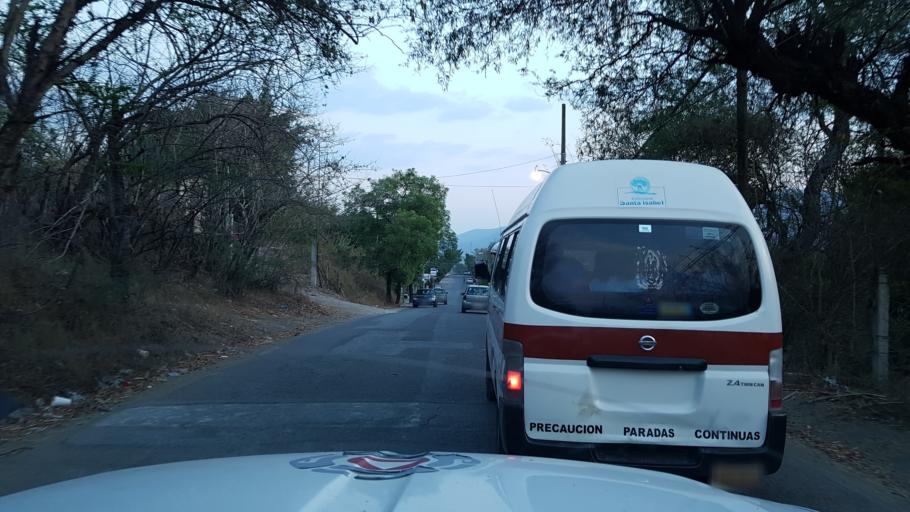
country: MX
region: Morelos
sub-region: Tlaltizapan de Zapata
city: Colonia Palo Prieto (Chipitongo)
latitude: 18.7024
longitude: -99.1061
